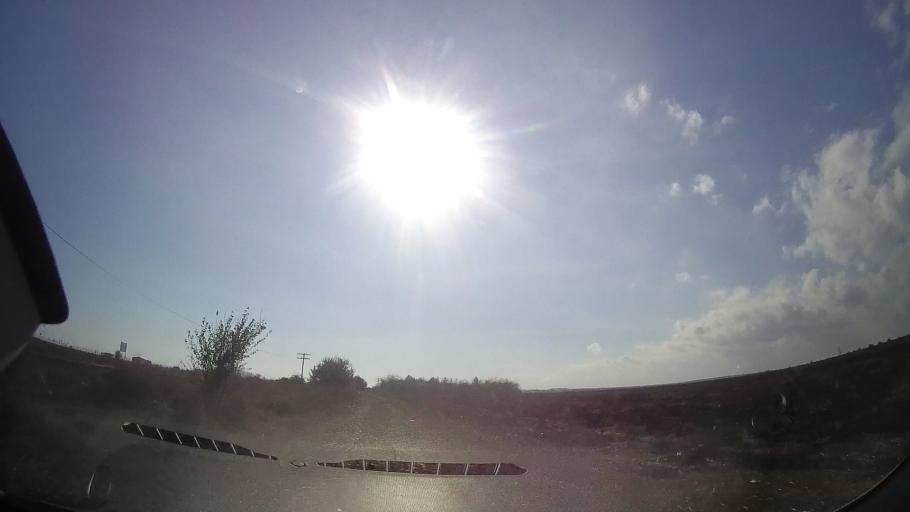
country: RO
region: Constanta
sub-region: Comuna Tuzla
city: Tuzla
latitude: 43.9750
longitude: 28.6440
